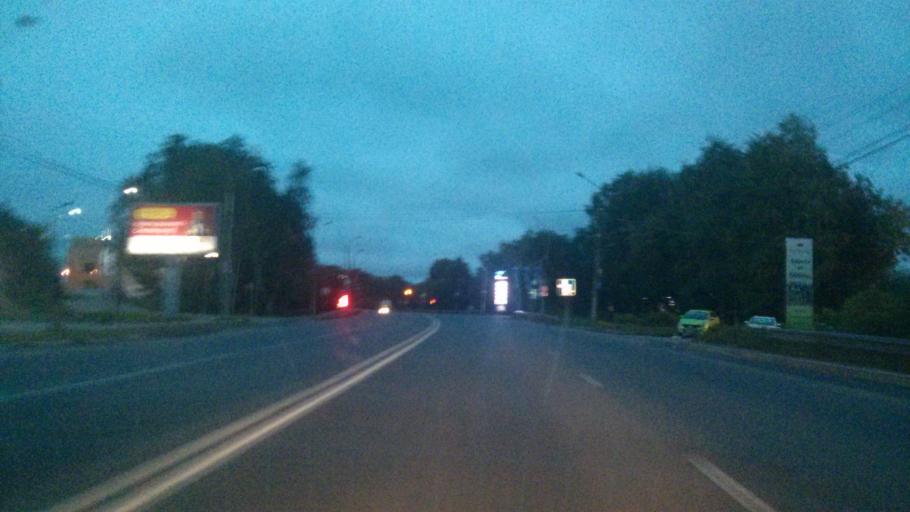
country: RU
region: Nizjnij Novgorod
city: Nizhniy Novgorod
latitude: 56.2250
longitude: 43.9404
